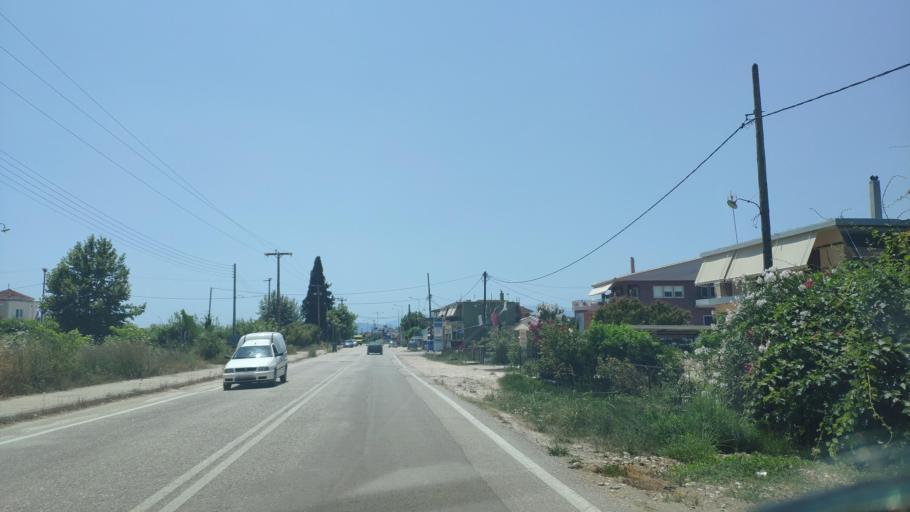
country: GR
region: Epirus
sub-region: Nomos Artas
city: Neochori
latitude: 39.0733
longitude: 21.0219
